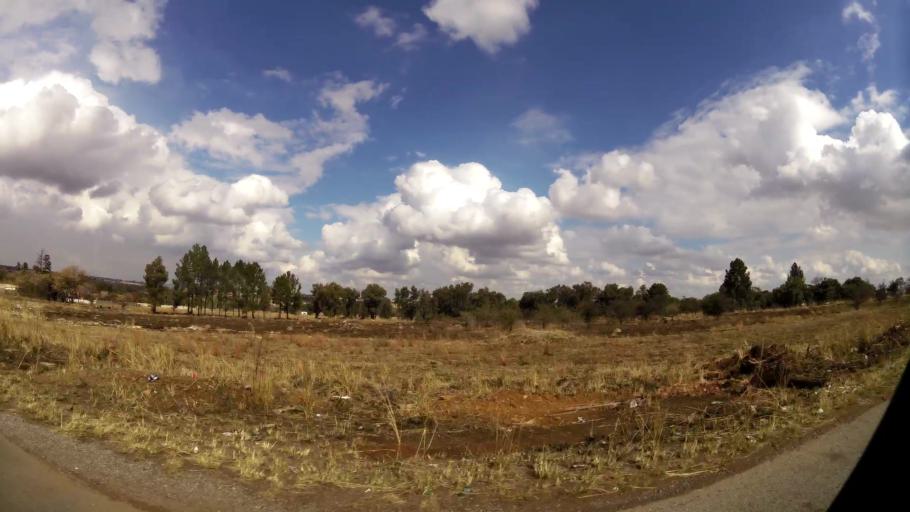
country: ZA
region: Gauteng
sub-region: Sedibeng District Municipality
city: Vanderbijlpark
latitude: -26.7405
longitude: 27.8214
